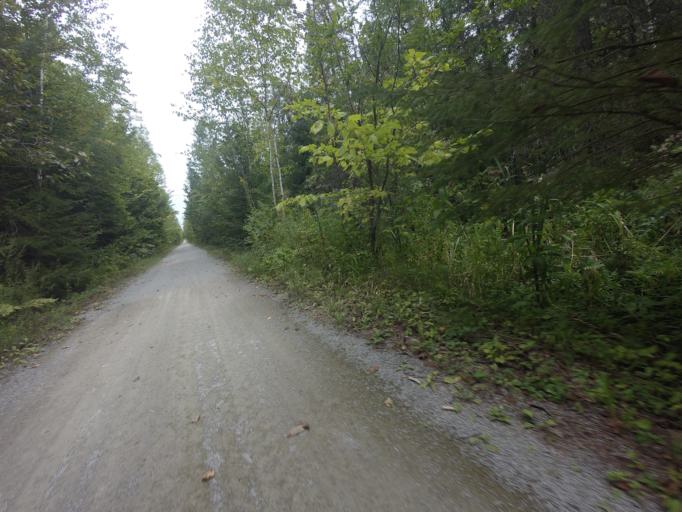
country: CA
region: Ontario
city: Uxbridge
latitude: 44.2644
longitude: -79.0241
